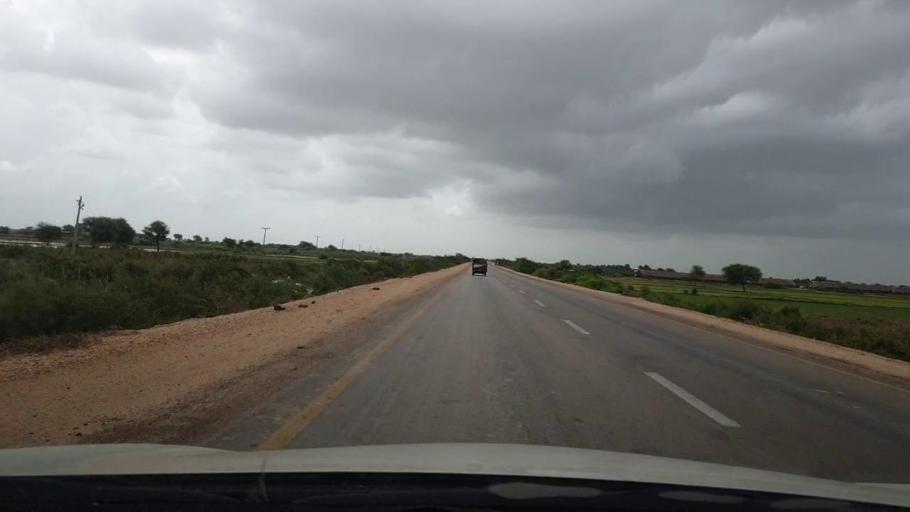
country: PK
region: Sindh
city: Mirpur Batoro
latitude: 24.6438
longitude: 68.4329
